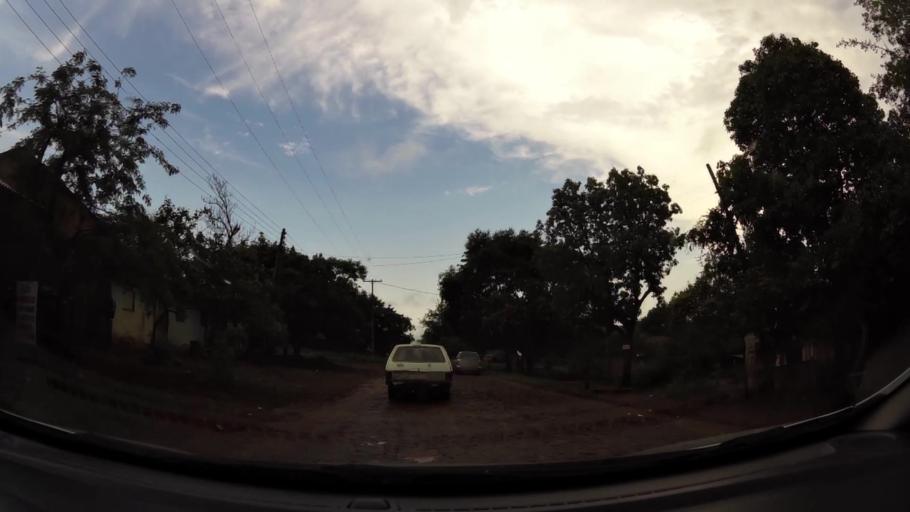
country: PY
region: Alto Parana
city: Presidente Franco
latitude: -25.5342
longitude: -54.6667
